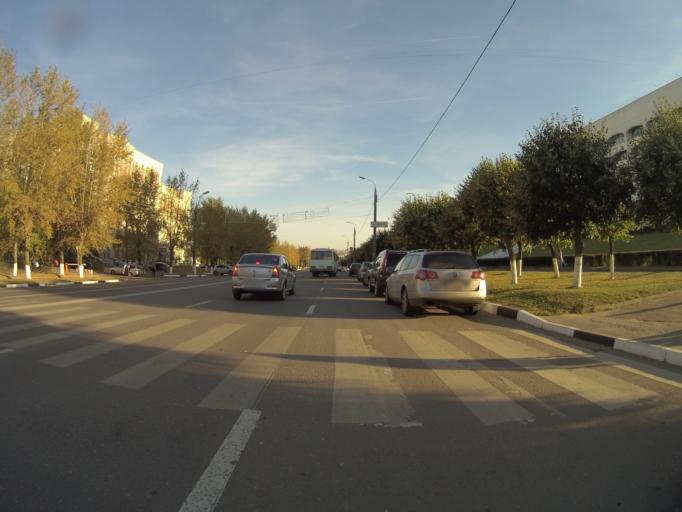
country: RU
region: Vladimir
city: Vladimir
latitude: 56.1384
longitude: 40.3903
